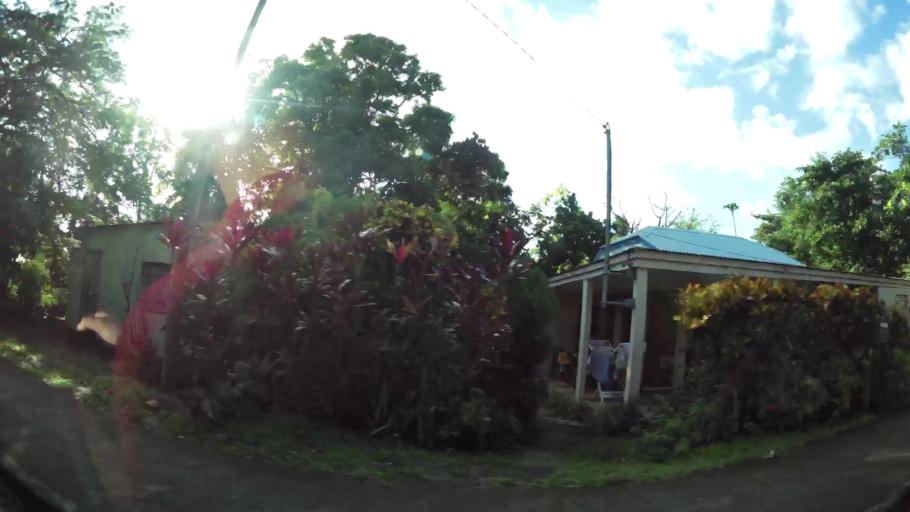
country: GP
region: Guadeloupe
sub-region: Guadeloupe
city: Pointe-Noire
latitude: 16.2802
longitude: -61.8020
